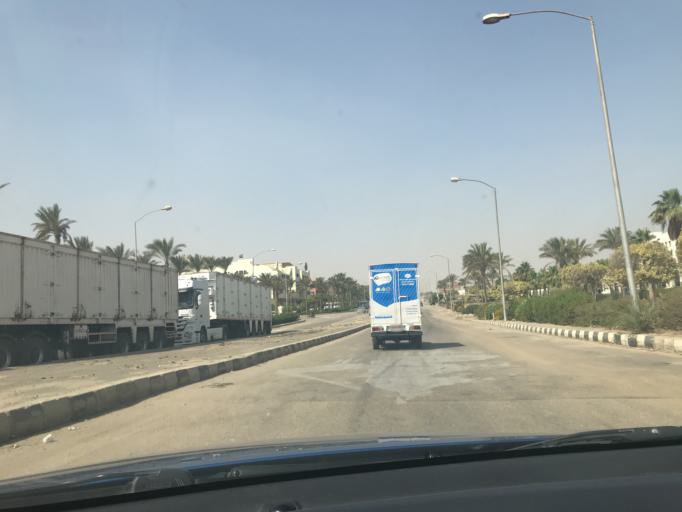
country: EG
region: Eastern Province
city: Bilbays
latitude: 30.2483
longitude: 31.7609
